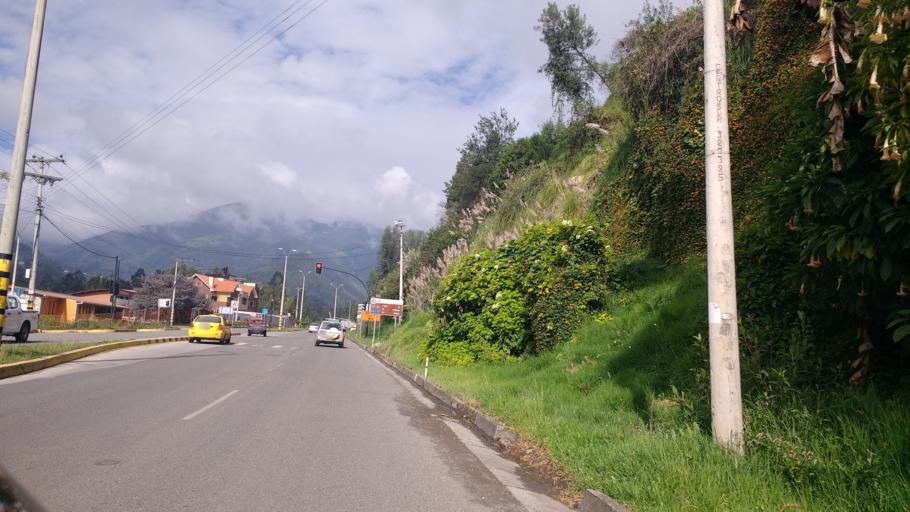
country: EC
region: Azuay
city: Cuenca
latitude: -2.8996
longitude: -79.0487
